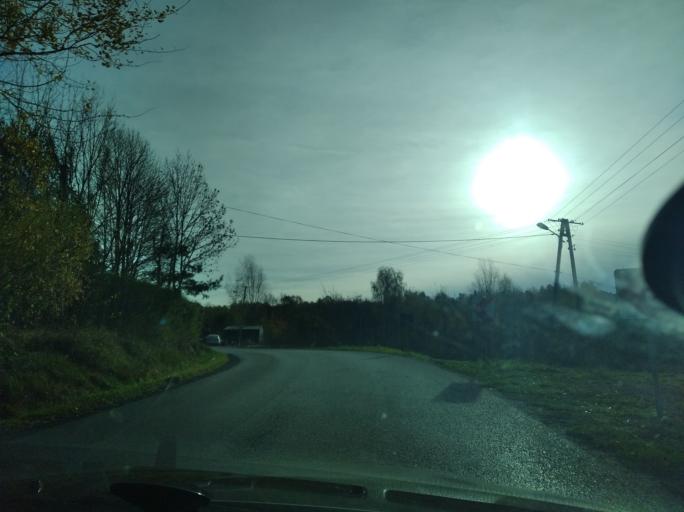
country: PL
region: Subcarpathian Voivodeship
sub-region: Powiat rzeszowski
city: Tyczyn
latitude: 49.9945
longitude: 22.0601
